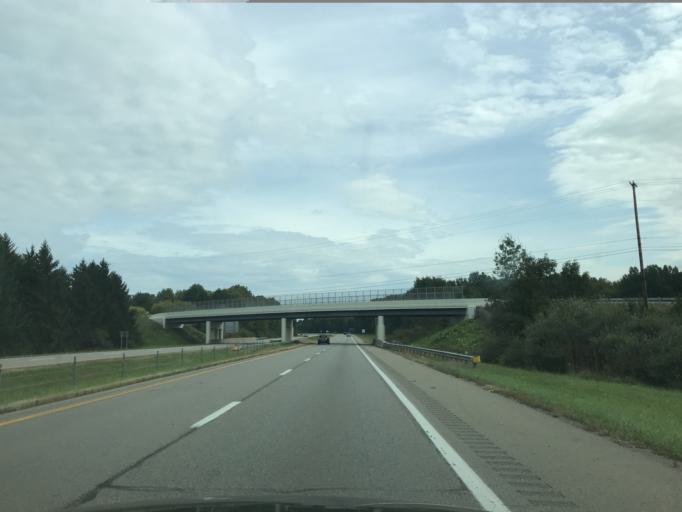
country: US
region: Ohio
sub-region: Trumbull County
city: Leavittsburg
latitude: 41.2681
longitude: -80.8689
